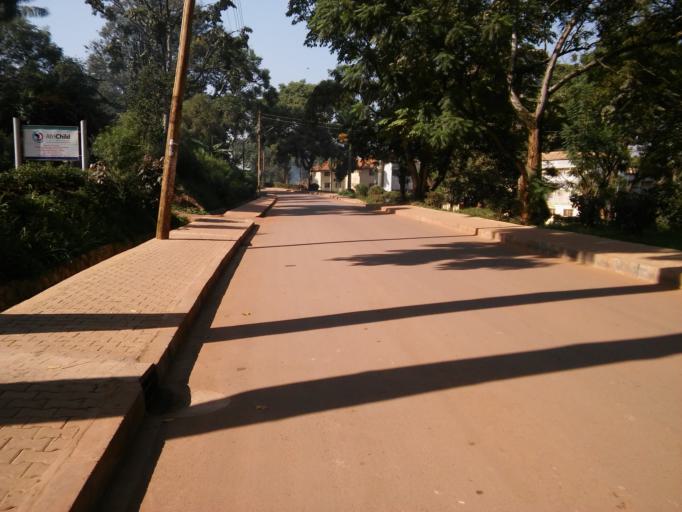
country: UG
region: Central Region
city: Kampala Central Division
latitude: 0.3319
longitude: 32.5666
